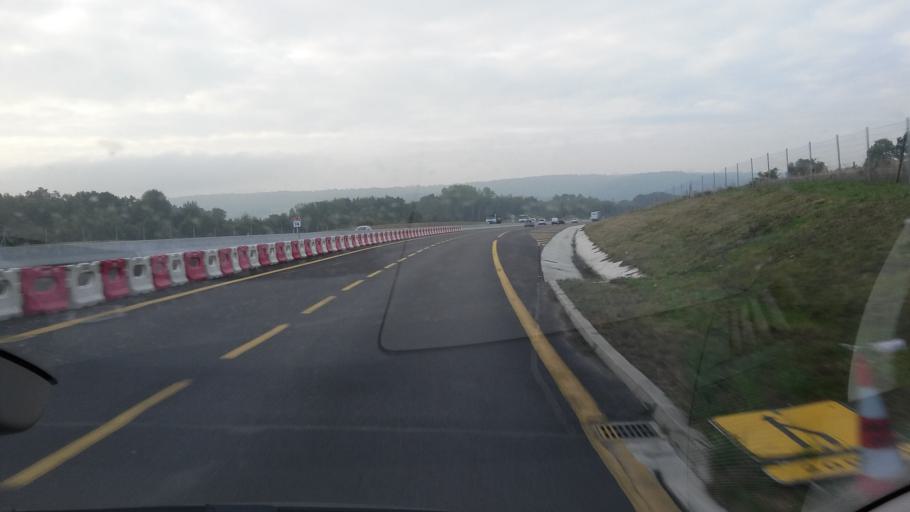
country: FR
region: Champagne-Ardenne
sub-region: Departement des Ardennes
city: La Francheville
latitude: 49.7152
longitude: 4.7001
